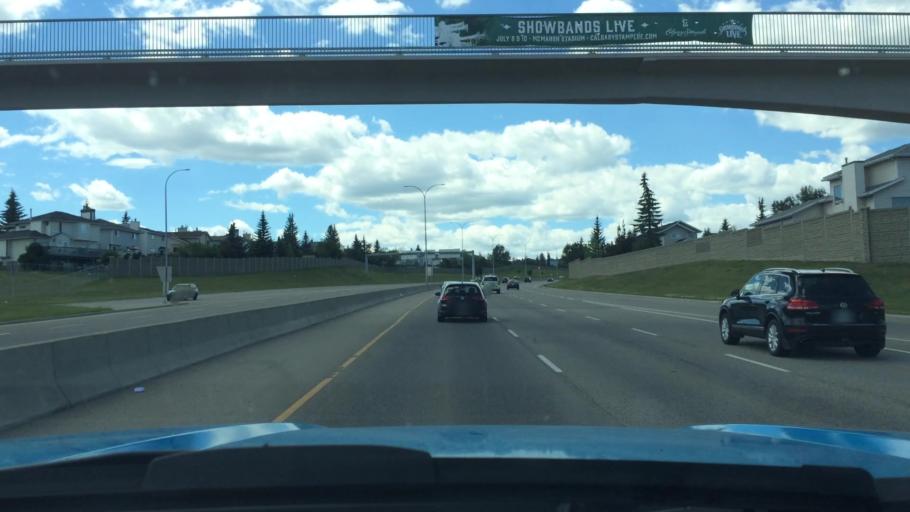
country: CA
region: Alberta
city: Calgary
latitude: 51.1432
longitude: -114.0958
